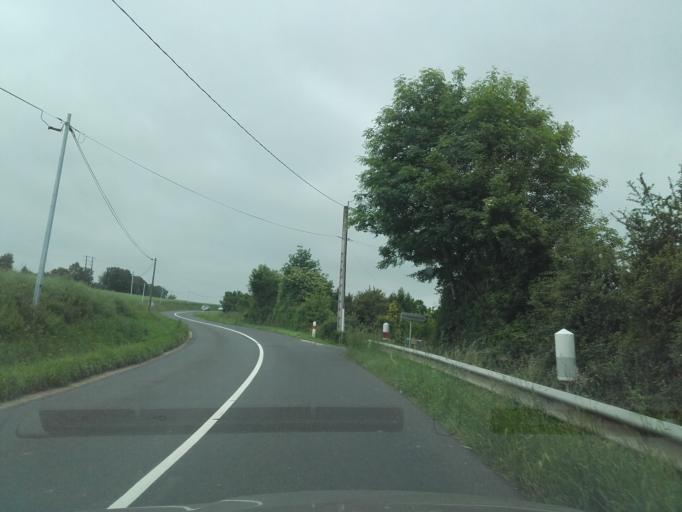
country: FR
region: Centre
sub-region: Departement du Loir-et-Cher
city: Savigny-sur-Braye
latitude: 47.8849
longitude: 0.7968
